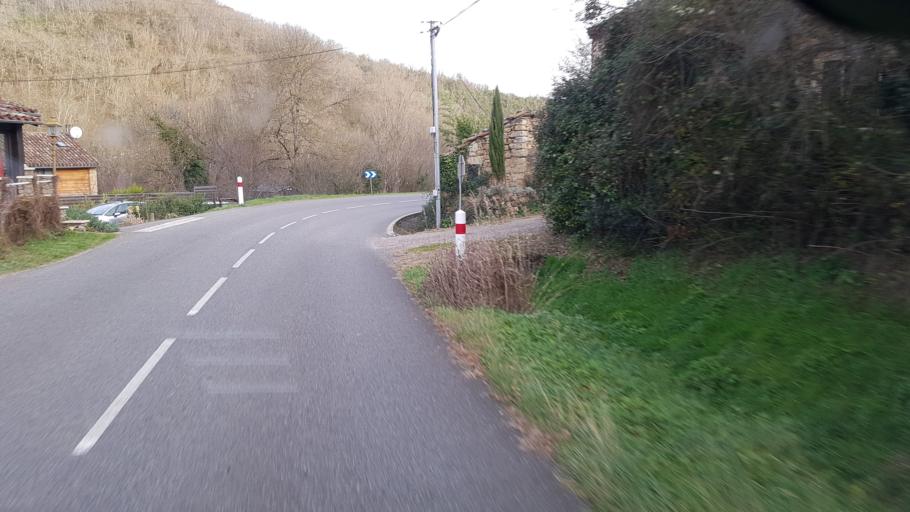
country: FR
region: Midi-Pyrenees
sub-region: Departement du Tarn-et-Garonne
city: Montricoux
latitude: 44.0445
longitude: 1.6709
